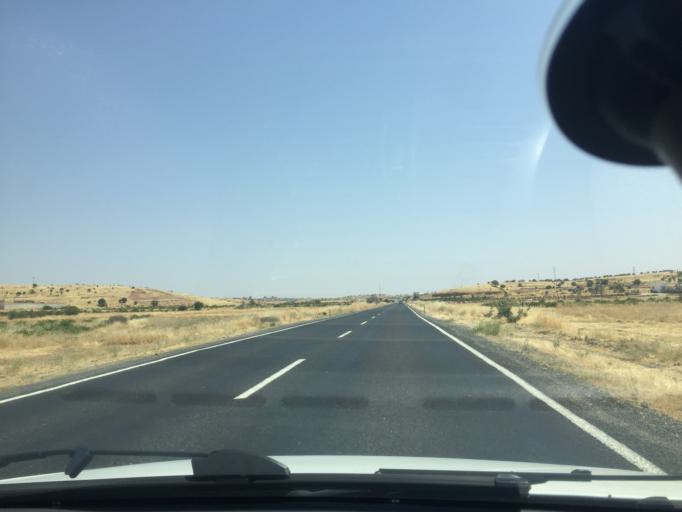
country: TR
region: Mardin
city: Kindirip
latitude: 37.4535
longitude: 41.2537
